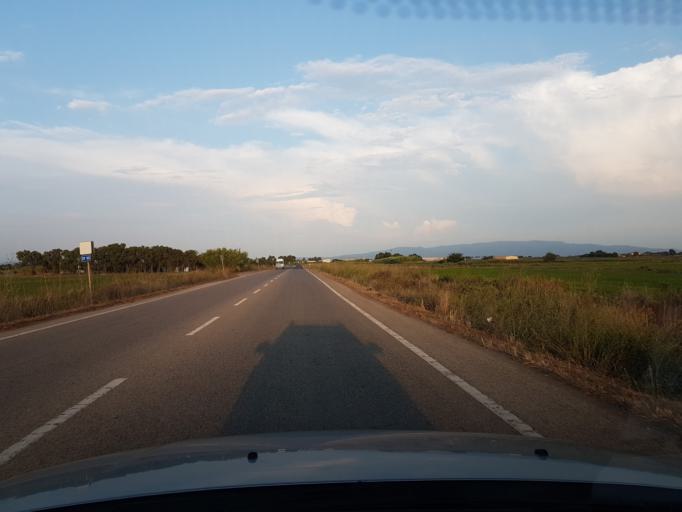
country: IT
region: Sardinia
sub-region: Provincia di Oristano
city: Cabras
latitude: 39.9188
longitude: 8.5236
